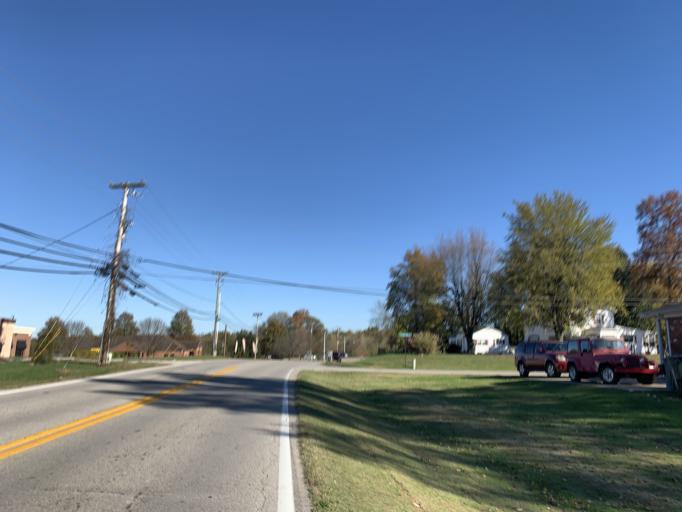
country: US
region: Kentucky
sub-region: Jefferson County
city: Pleasure Ridge Park
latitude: 38.1474
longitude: -85.8888
